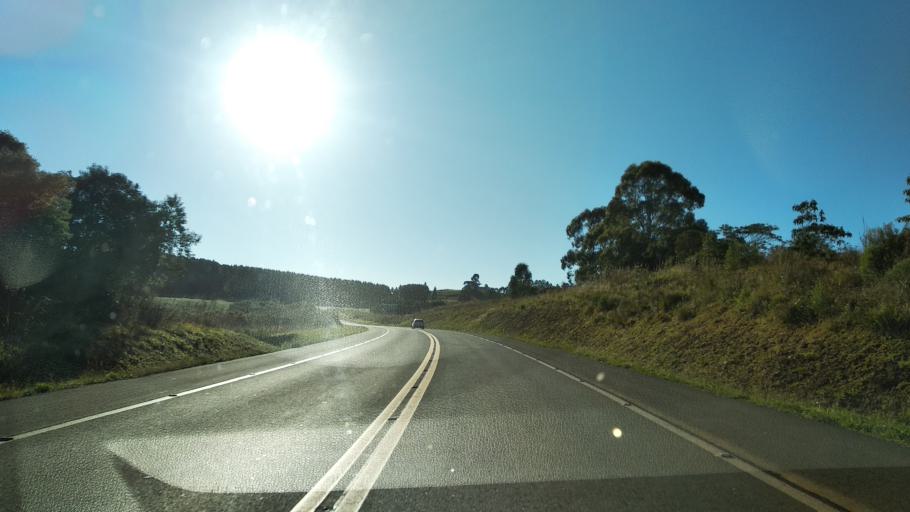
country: BR
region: Santa Catarina
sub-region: Lages
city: Lages
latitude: -27.7912
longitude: -50.4148
